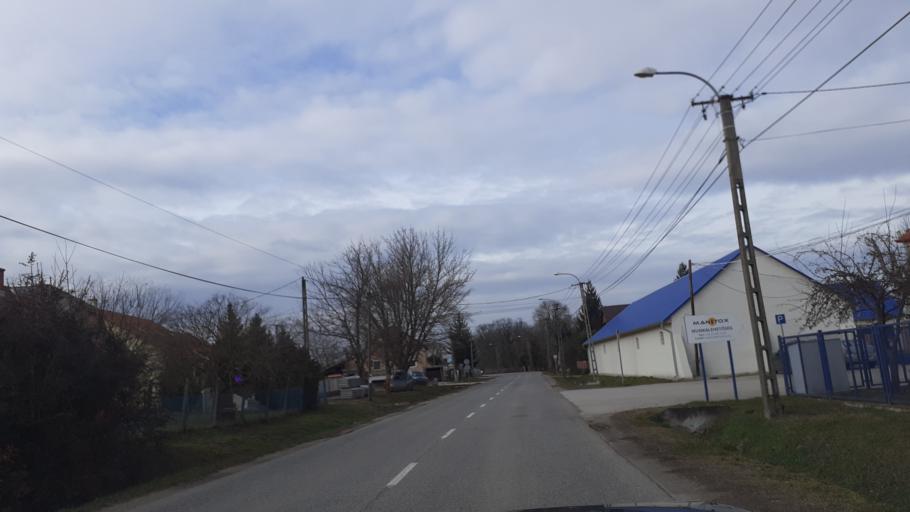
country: HU
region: Fejer
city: Szabadbattyan
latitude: 47.0818
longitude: 18.4083
